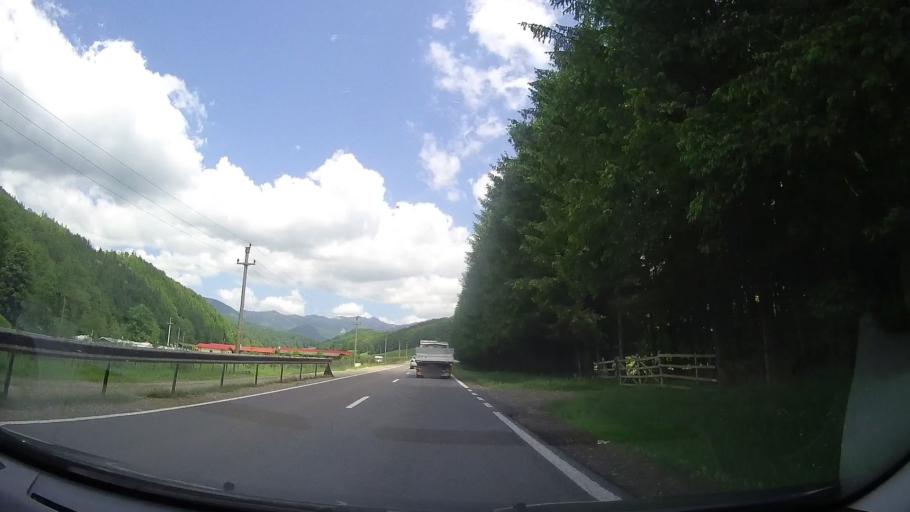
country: RO
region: Prahova
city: Maneciu
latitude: 45.4171
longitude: 25.9429
